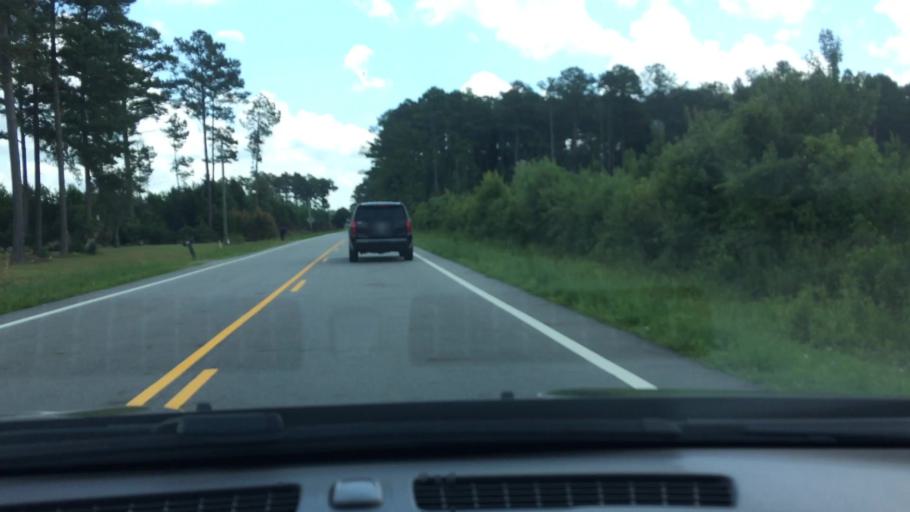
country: US
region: North Carolina
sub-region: Craven County
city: Vanceboro
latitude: 35.4291
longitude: -77.2028
